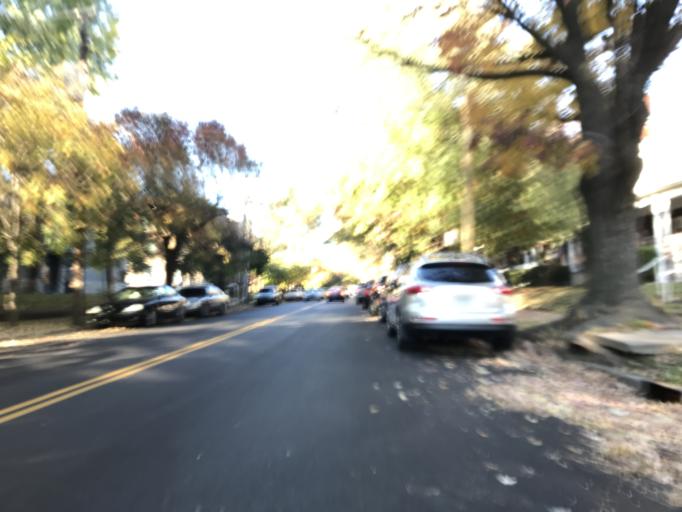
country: US
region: Kentucky
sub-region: Jefferson County
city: Louisville
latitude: 38.2237
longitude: -85.7623
